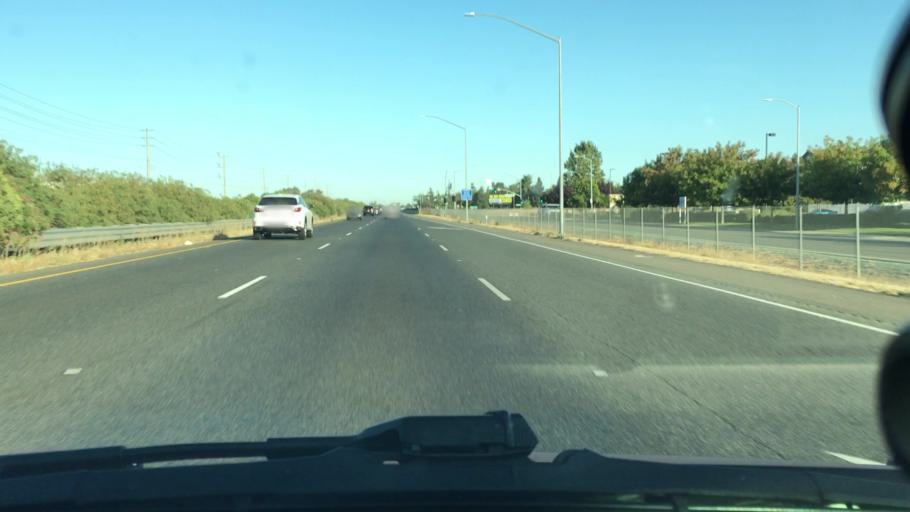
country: US
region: California
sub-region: Sacramento County
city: Elk Grove
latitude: 38.3832
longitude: -121.3685
